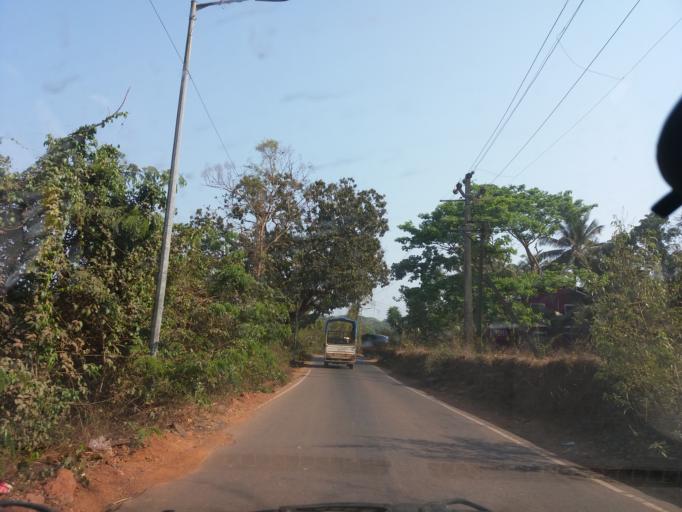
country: IN
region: Goa
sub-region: North Goa
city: Queula
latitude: 15.3495
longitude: 73.9794
